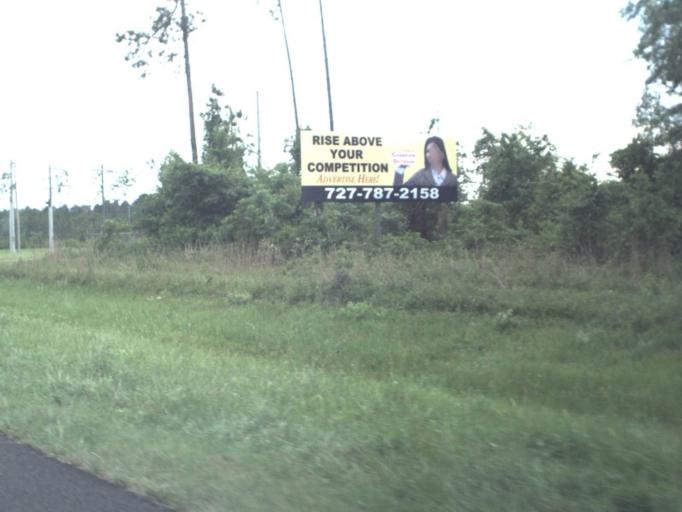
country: US
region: Florida
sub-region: Duval County
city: Baldwin
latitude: 30.1833
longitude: -82.0218
